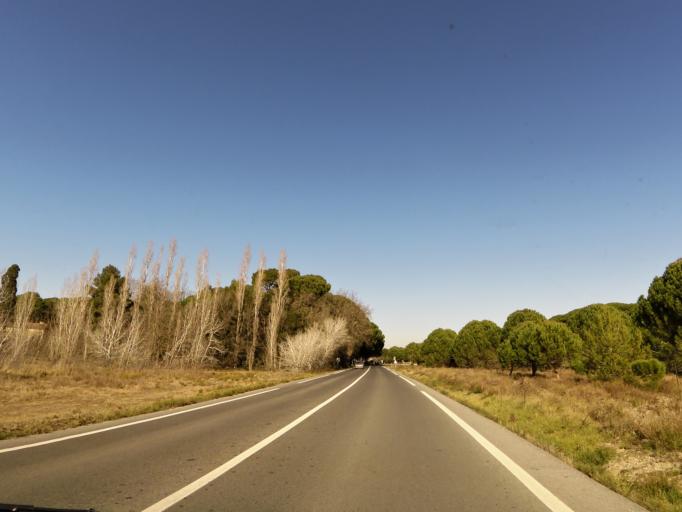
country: FR
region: Languedoc-Roussillon
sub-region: Departement du Gard
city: Aigues-Mortes
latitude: 43.5836
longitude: 4.2083
